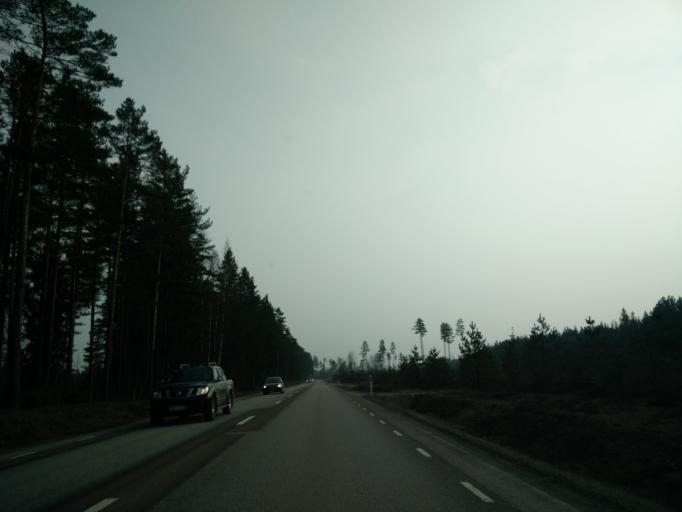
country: SE
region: Vaermland
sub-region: Forshaga Kommun
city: Forshaga
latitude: 59.5043
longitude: 13.4352
